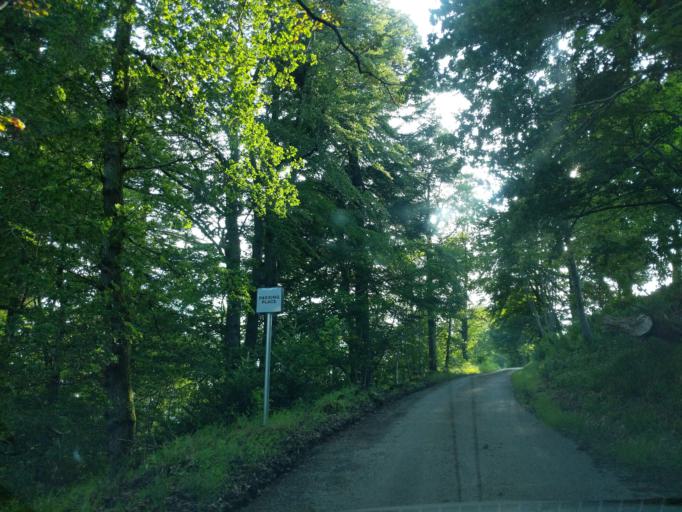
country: GB
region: Scotland
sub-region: Moray
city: Dufftown
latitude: 57.4777
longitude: -3.0678
